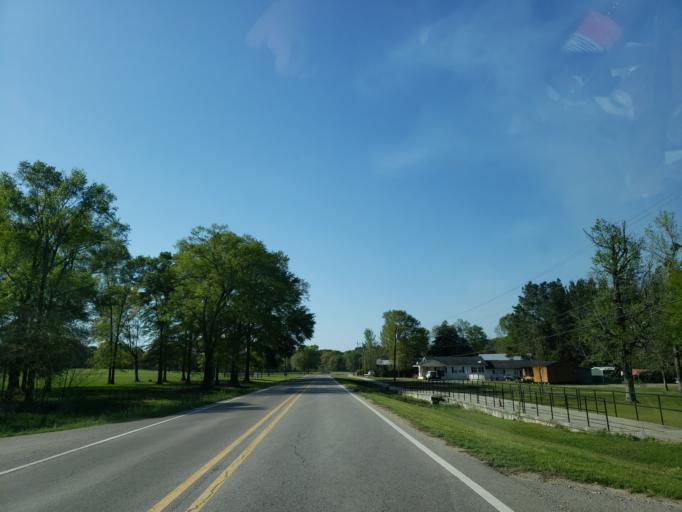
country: US
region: Mississippi
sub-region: Perry County
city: Richton
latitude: 31.3366
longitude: -88.9343
